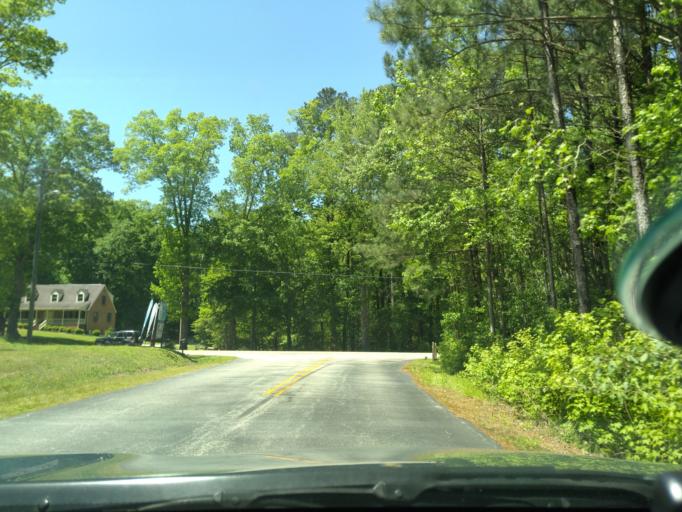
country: US
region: Virginia
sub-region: Prince George County
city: Prince George
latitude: 37.2159
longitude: -77.3099
